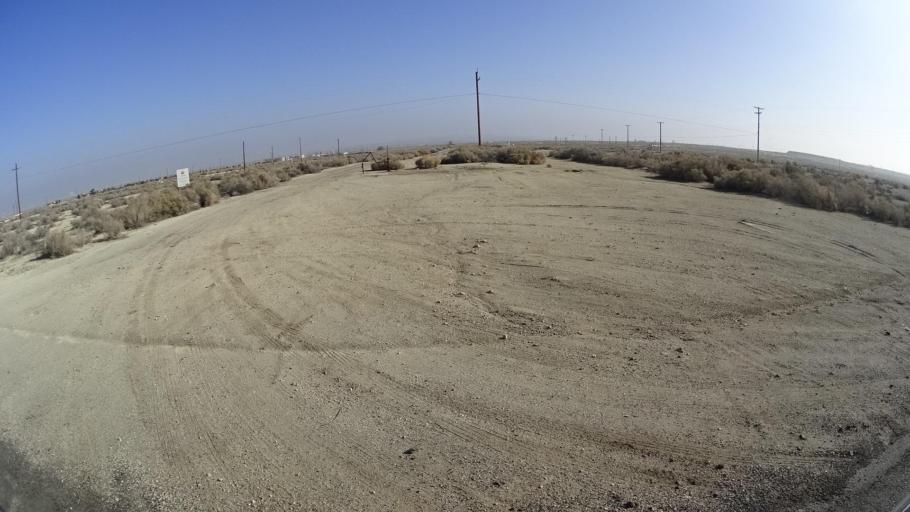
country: US
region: California
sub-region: Kern County
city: Taft Heights
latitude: 35.2013
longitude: -119.5687
